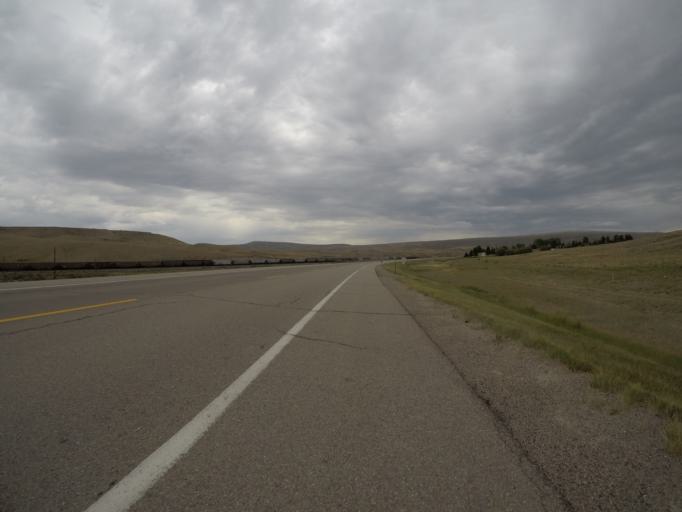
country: US
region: Wyoming
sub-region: Lincoln County
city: Kemmerer
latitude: 41.8006
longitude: -110.5582
